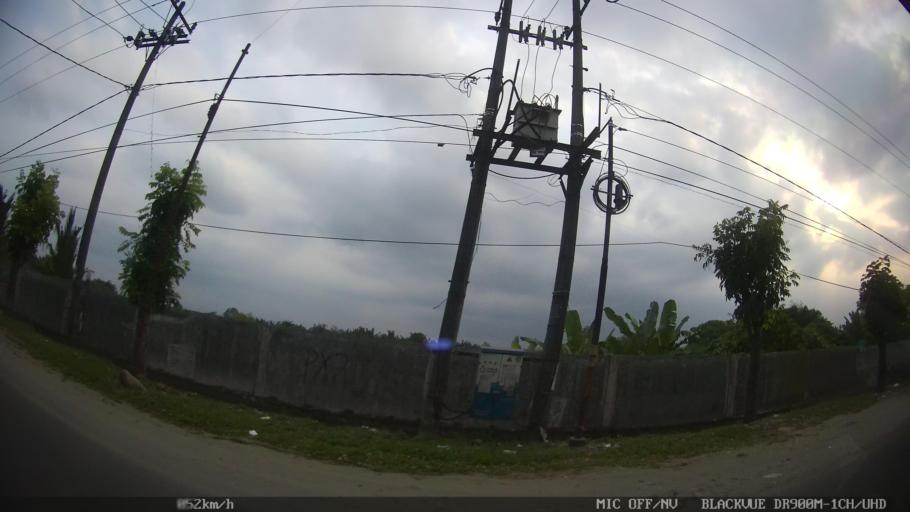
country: ID
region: North Sumatra
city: Sunggal
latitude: 3.5669
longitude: 98.6149
